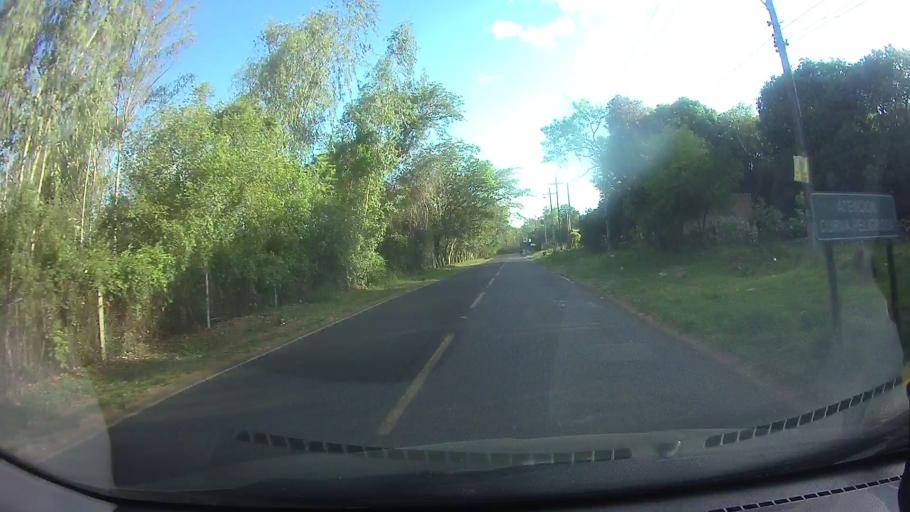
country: PY
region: Cordillera
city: Emboscada
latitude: -25.1931
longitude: -57.3188
